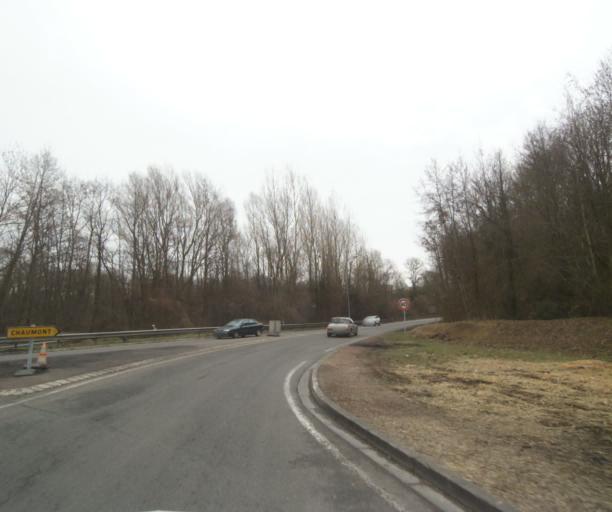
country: FR
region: Lorraine
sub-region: Departement de la Meuse
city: Ancerville
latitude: 48.6225
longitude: 4.9935
